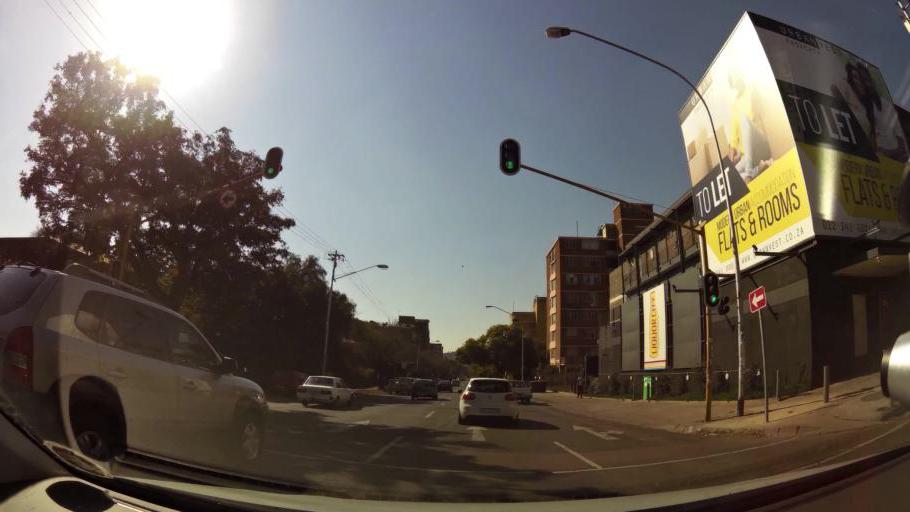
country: ZA
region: Gauteng
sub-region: City of Tshwane Metropolitan Municipality
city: Pretoria
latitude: -25.7561
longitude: 28.2012
